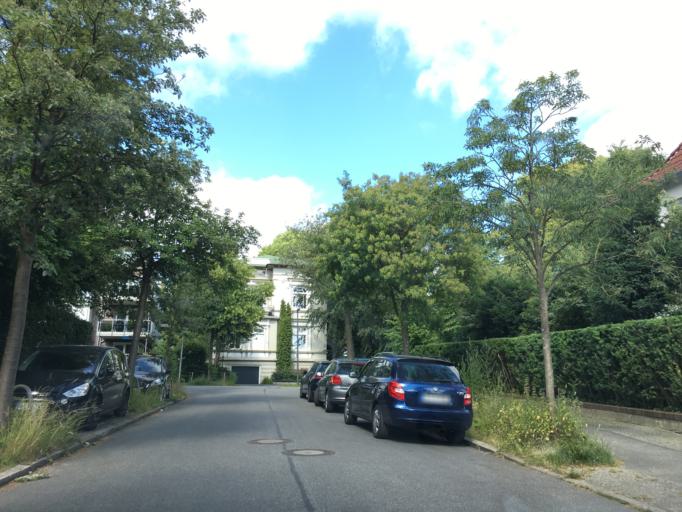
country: DE
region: Schleswig-Holstein
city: Kiel
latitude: 54.3391
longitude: 10.1482
